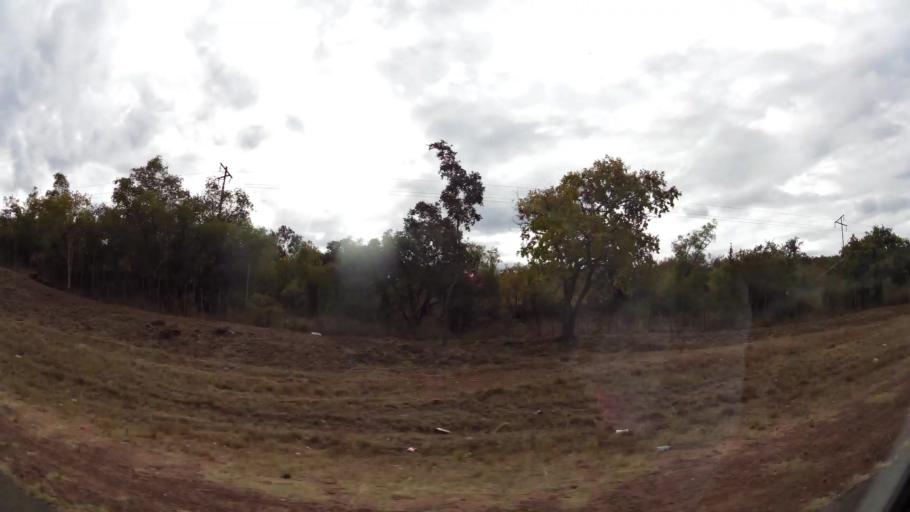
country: ZA
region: Limpopo
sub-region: Waterberg District Municipality
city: Modimolle
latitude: -24.6716
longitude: 28.4516
